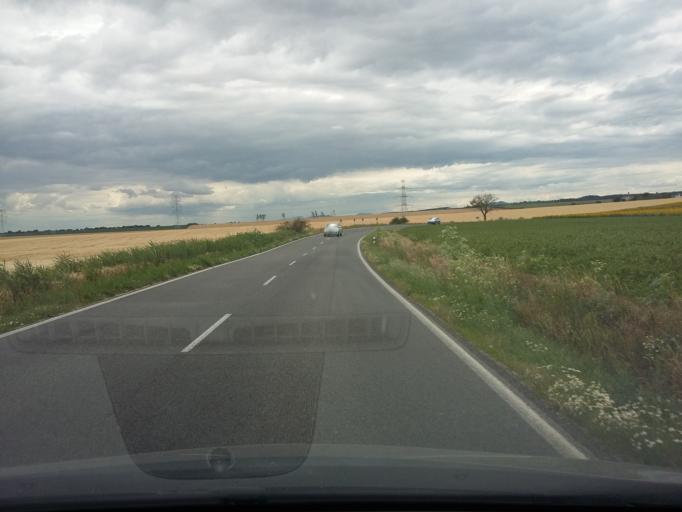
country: SK
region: Trnavsky
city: Vrbove
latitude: 48.6015
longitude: 17.7000
